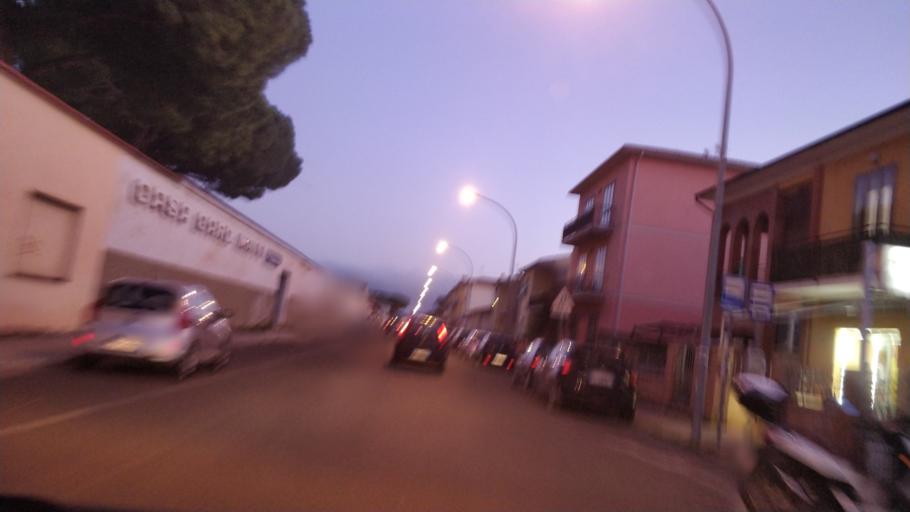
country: IT
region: Tuscany
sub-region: Provincia di Livorno
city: S.P. in Palazzi
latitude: 43.3281
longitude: 10.5040
